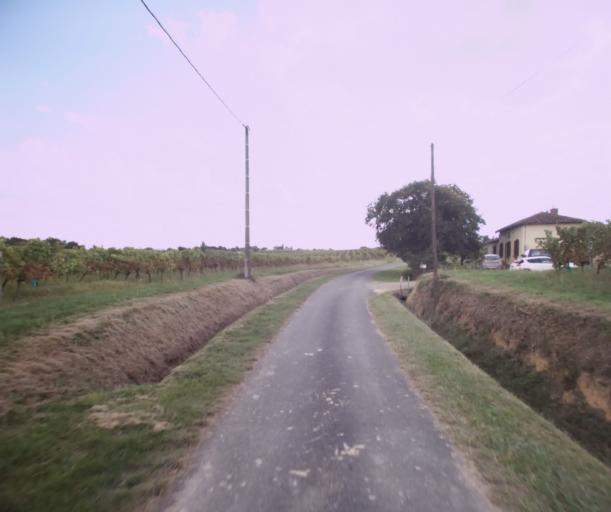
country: FR
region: Midi-Pyrenees
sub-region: Departement du Gers
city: Cazaubon
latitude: 43.8936
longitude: -0.0534
